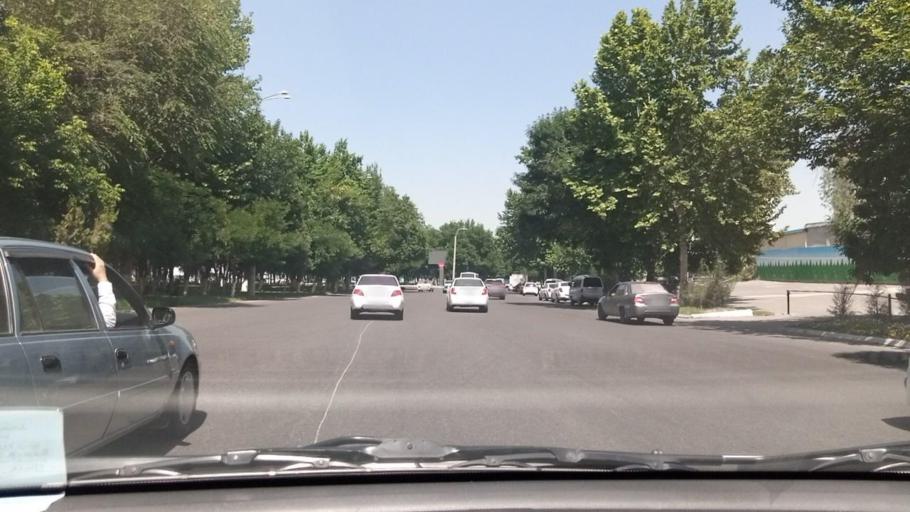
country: UZ
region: Toshkent Shahri
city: Tashkent
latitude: 41.2578
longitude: 69.2176
